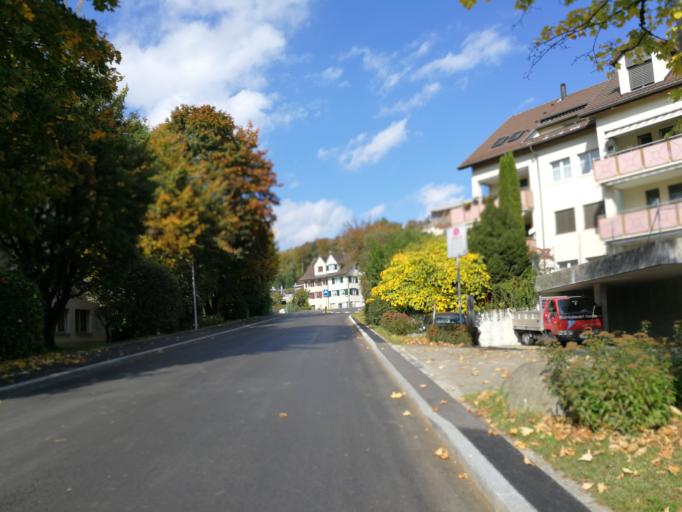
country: CH
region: Zurich
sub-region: Bezirk Meilen
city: Uetikon / Grossdorf
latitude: 47.2679
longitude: 8.6752
